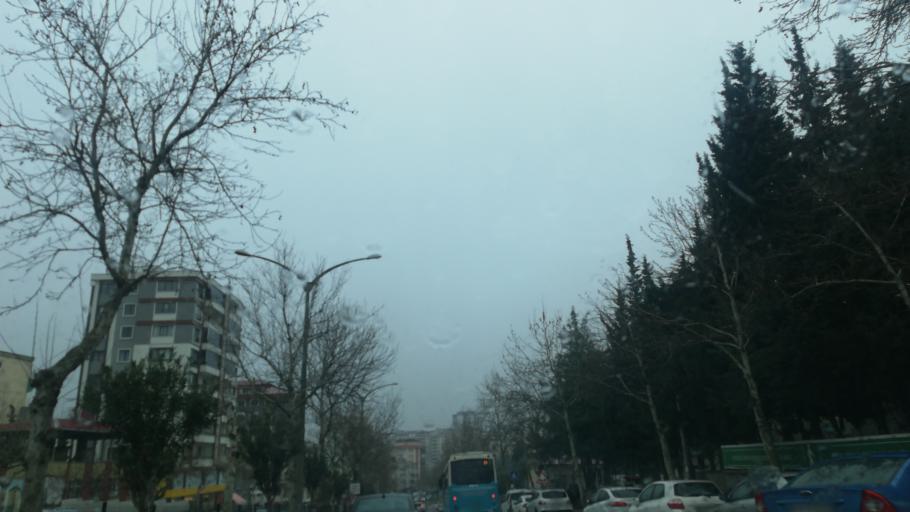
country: TR
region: Kahramanmaras
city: Kahramanmaras
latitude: 37.5887
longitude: 36.9031
